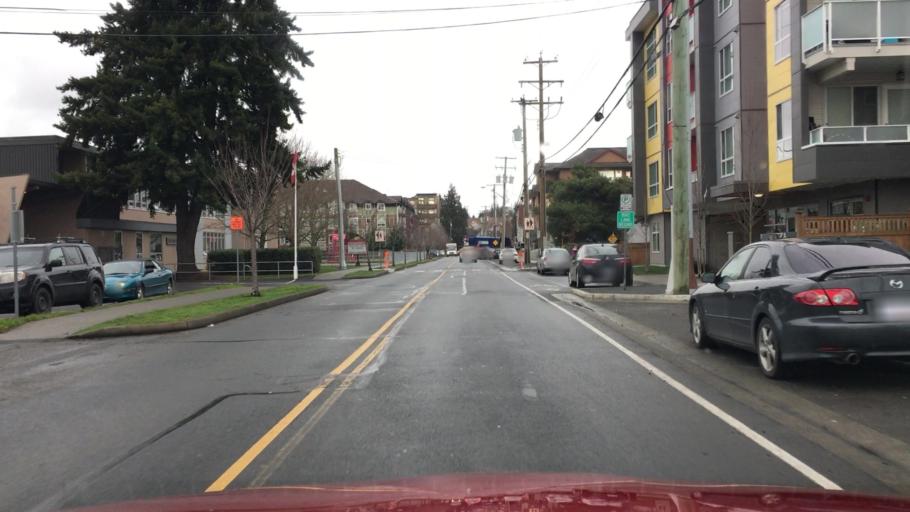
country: CA
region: British Columbia
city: Langford
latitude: 48.4514
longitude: -123.5050
